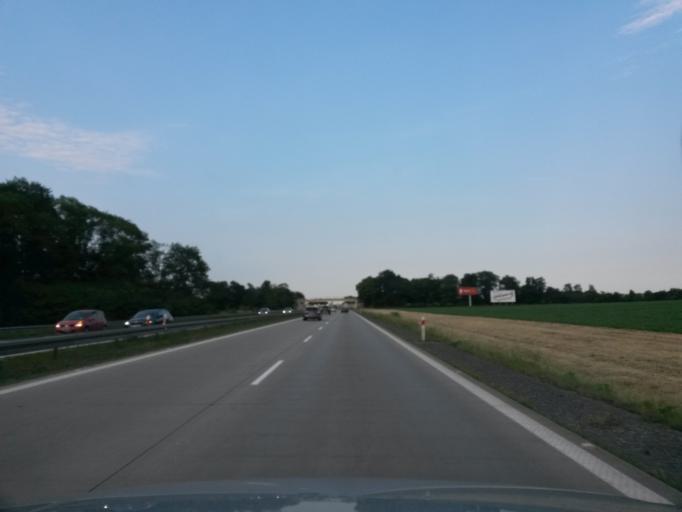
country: PL
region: Lower Silesian Voivodeship
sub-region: Powiat wroclawski
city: Gniechowice
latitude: 51.0349
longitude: 16.8496
